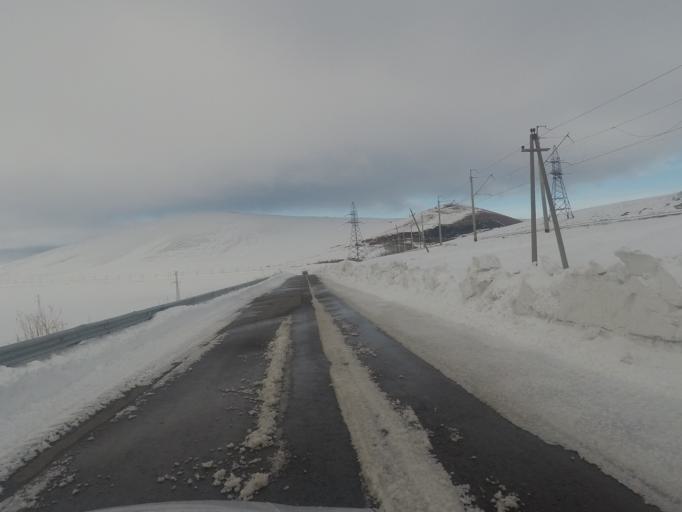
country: GE
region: Kvemo Kartli
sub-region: Tsalka
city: Tsalka
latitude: 41.4556
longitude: 43.8545
